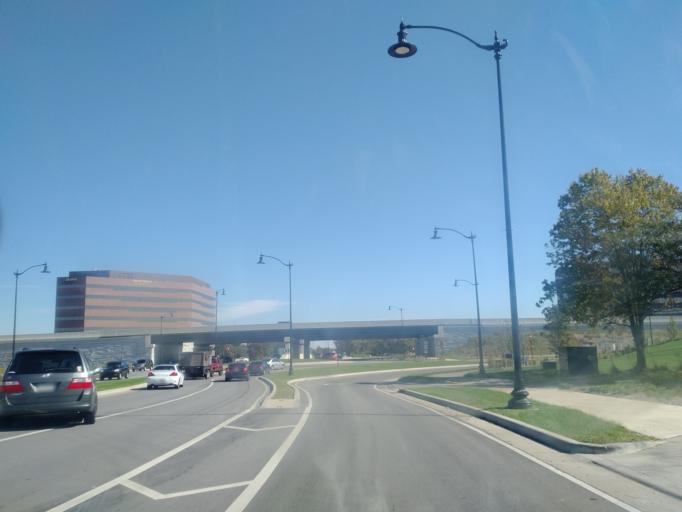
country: US
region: Indiana
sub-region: Hamilton County
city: Carmel
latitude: 39.9560
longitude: -86.1594
